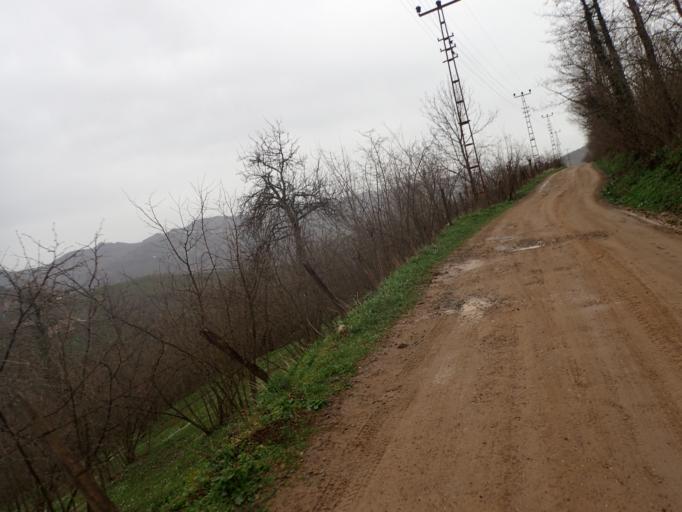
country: TR
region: Ordu
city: Camas
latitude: 40.8861
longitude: 37.4971
